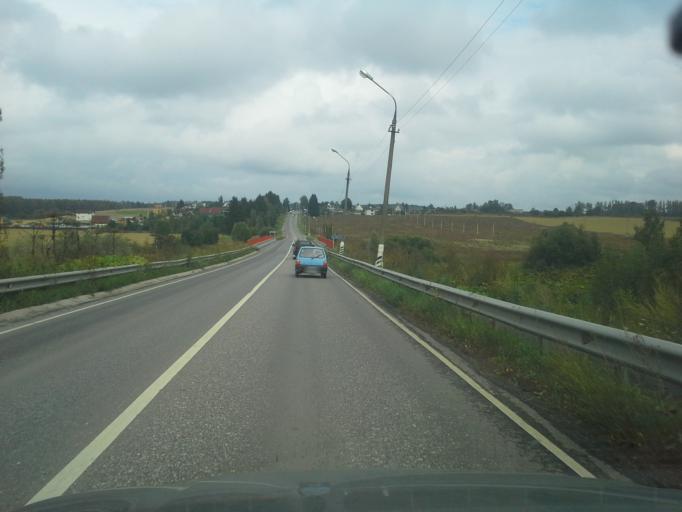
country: RU
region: Moskovskaya
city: Ruza
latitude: 55.7398
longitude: 36.1401
